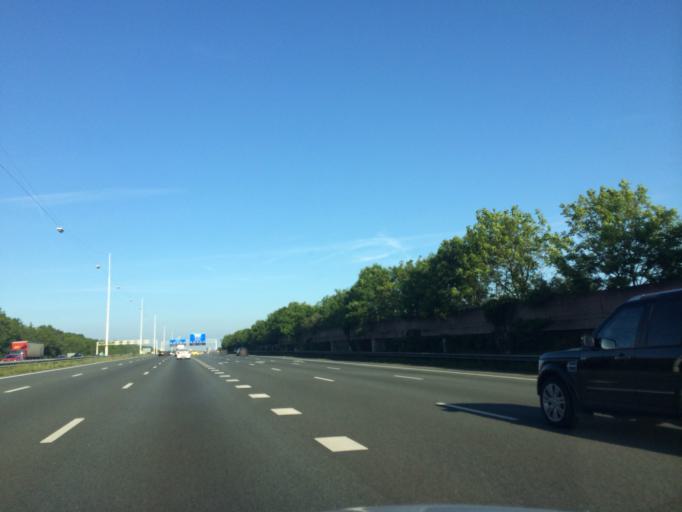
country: NL
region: Utrecht
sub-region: Gemeente IJsselstein
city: IJsselstein
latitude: 52.0699
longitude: 5.0495
